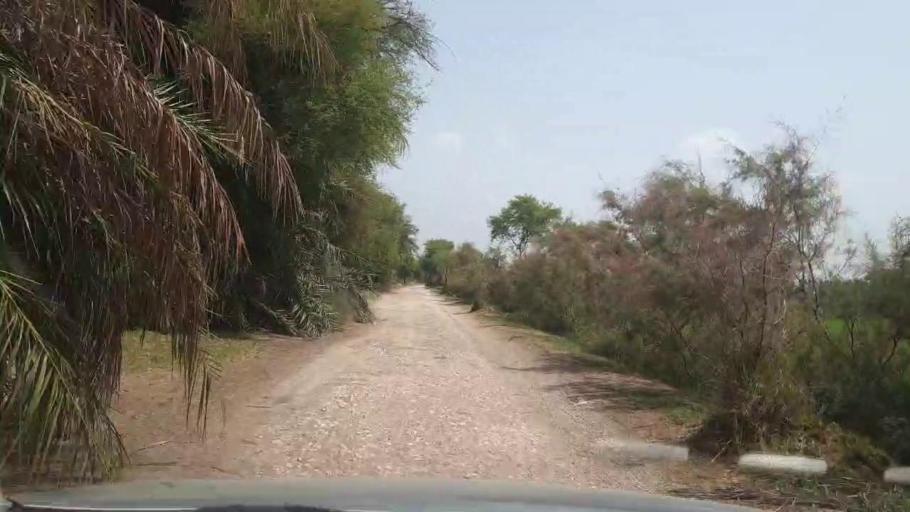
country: PK
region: Sindh
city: Garhi Yasin
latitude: 27.9341
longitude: 68.3655
